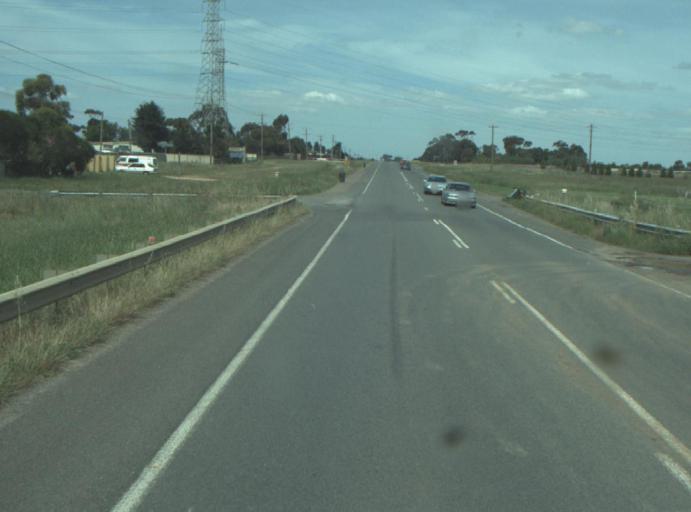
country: AU
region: Victoria
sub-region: Greater Geelong
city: Lara
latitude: -38.0324
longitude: 144.3549
